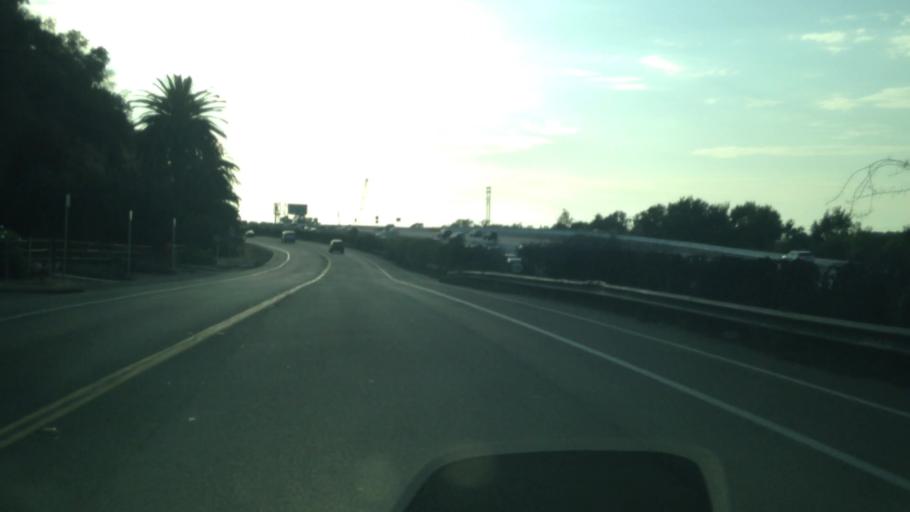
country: US
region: California
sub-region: San Diego County
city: San Diego
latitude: 32.7600
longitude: -117.1922
